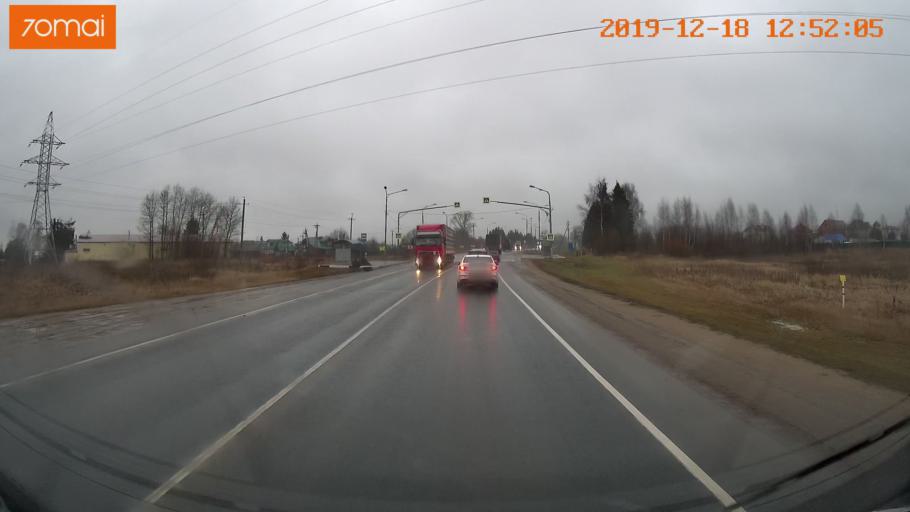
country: RU
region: Moskovskaya
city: Klin
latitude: 56.3093
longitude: 36.6863
